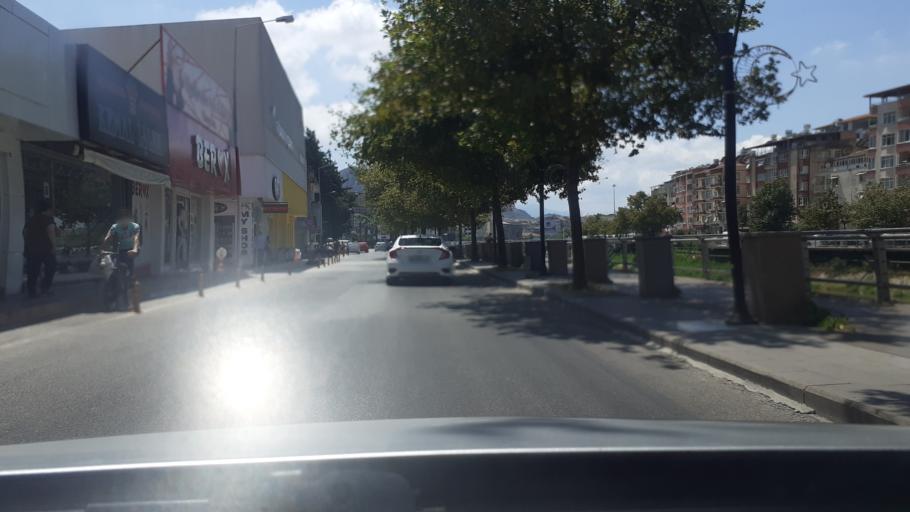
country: TR
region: Hatay
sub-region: Antakya Ilcesi
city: Antakya
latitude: 36.2060
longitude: 36.1621
